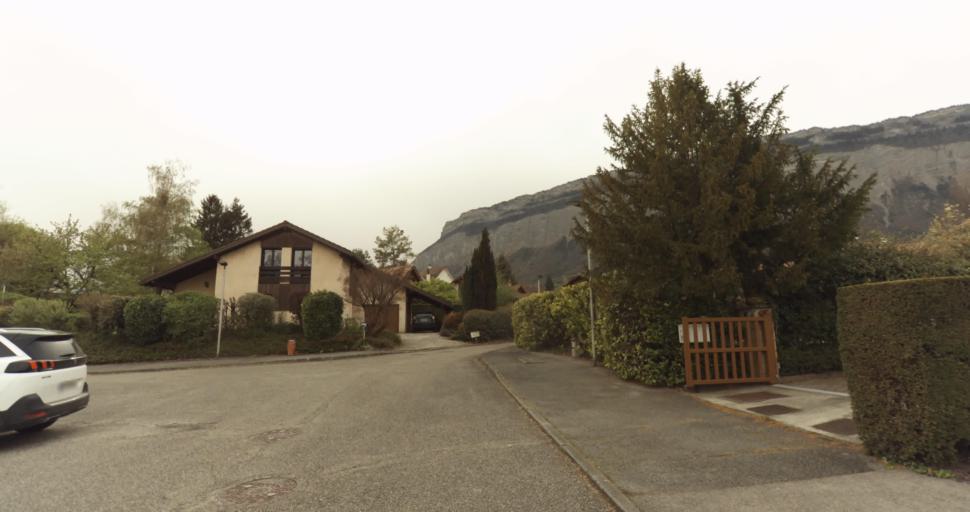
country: FR
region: Rhone-Alpes
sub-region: Departement de l'Isere
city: Biviers
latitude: 45.2349
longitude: 5.8161
